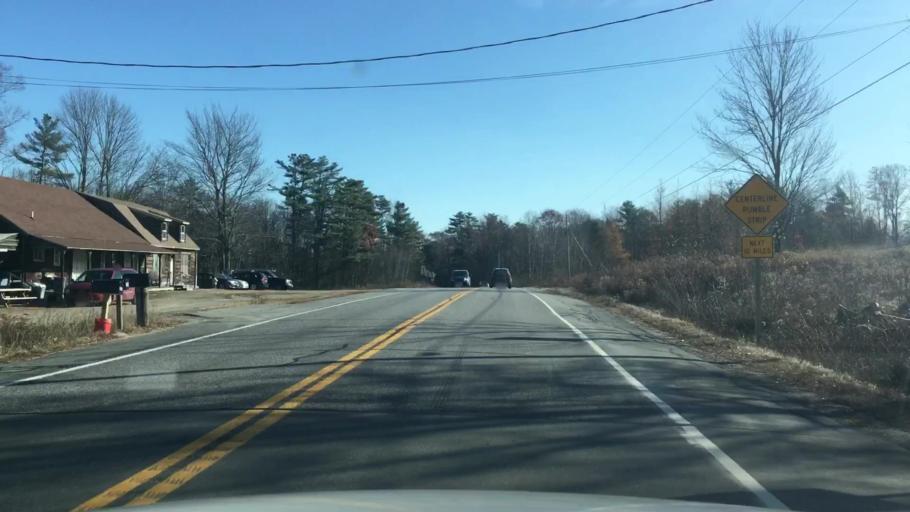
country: US
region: Maine
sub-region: Knox County
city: Washington
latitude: 44.2422
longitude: -69.3806
